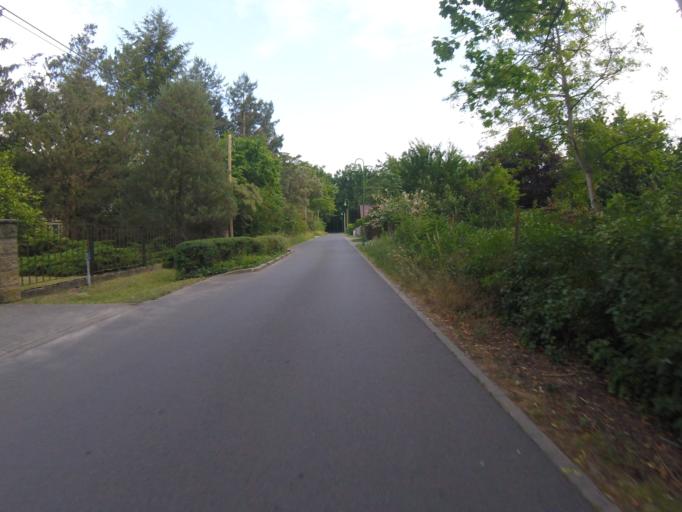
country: DE
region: Brandenburg
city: Konigs Wusterhausen
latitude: 52.2741
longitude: 13.6354
